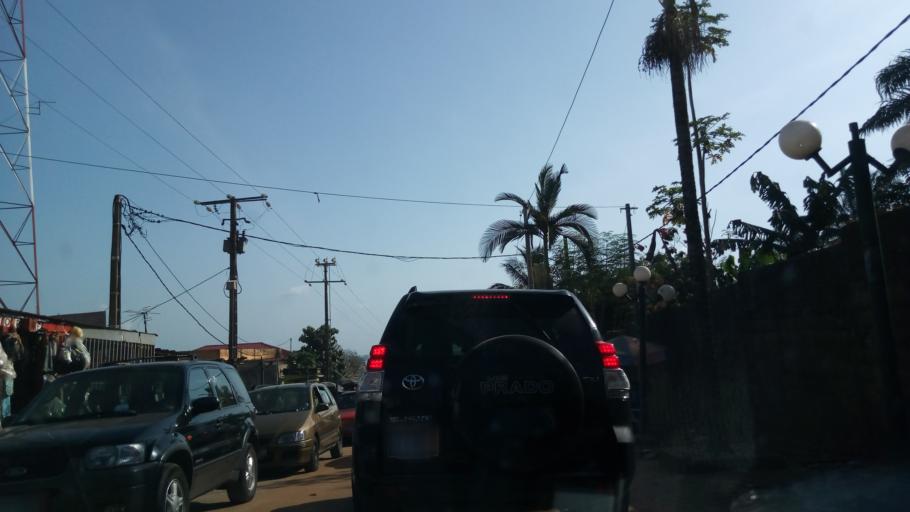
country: CI
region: Lagunes
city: Bingerville
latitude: 5.3585
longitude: -3.8906
